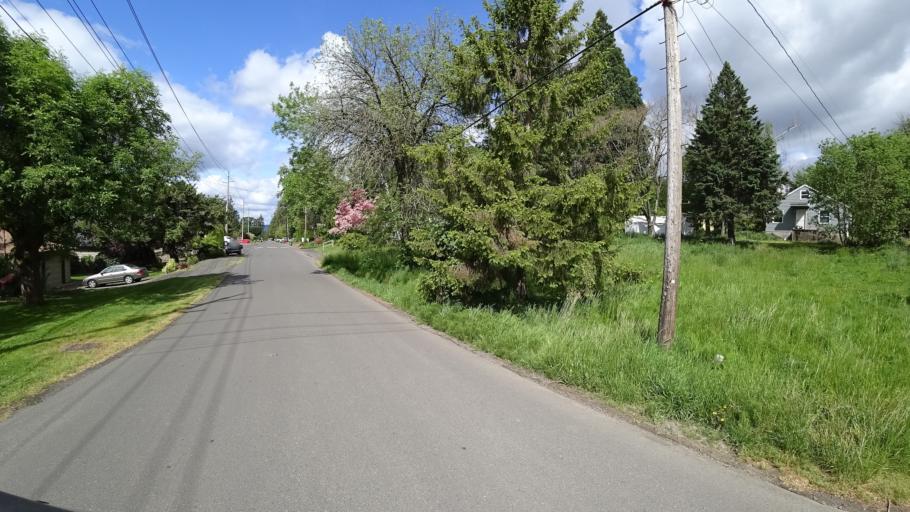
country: US
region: Oregon
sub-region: Washington County
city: Metzger
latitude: 45.4432
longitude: -122.7543
